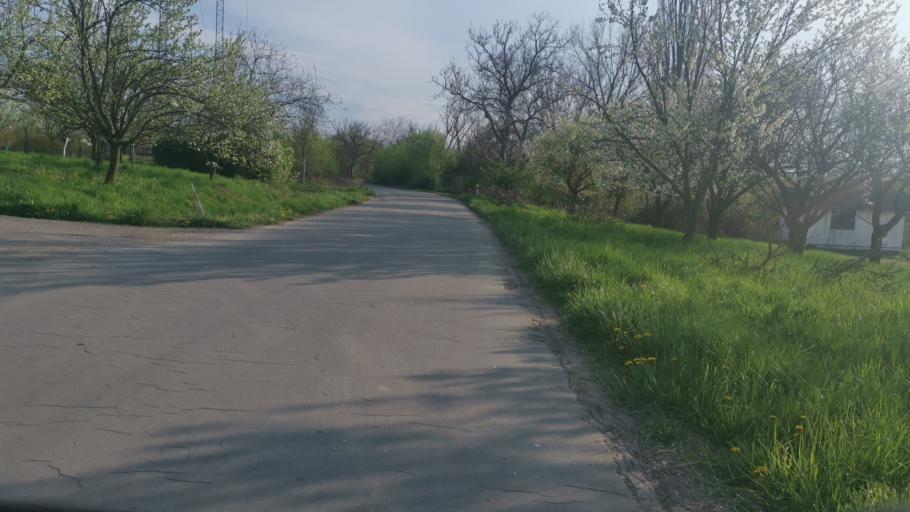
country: CZ
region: South Moravian
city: Petrov
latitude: 48.8568
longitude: 17.3070
